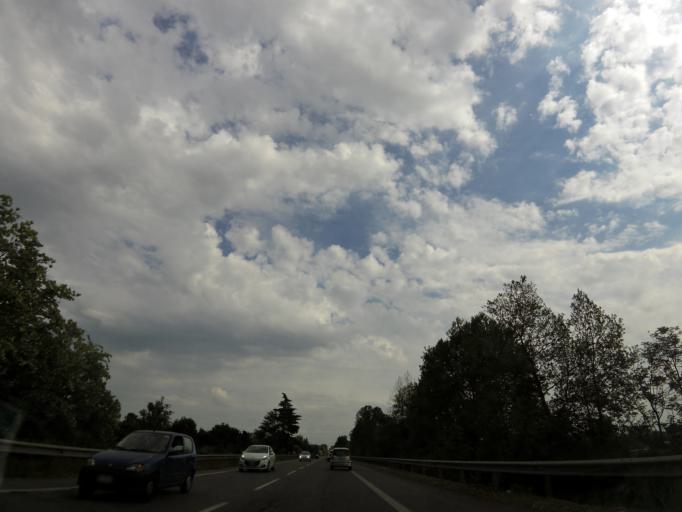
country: IT
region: Lombardy
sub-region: Citta metropolitana di Milano
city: Melegnano
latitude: 45.3739
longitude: 9.3090
